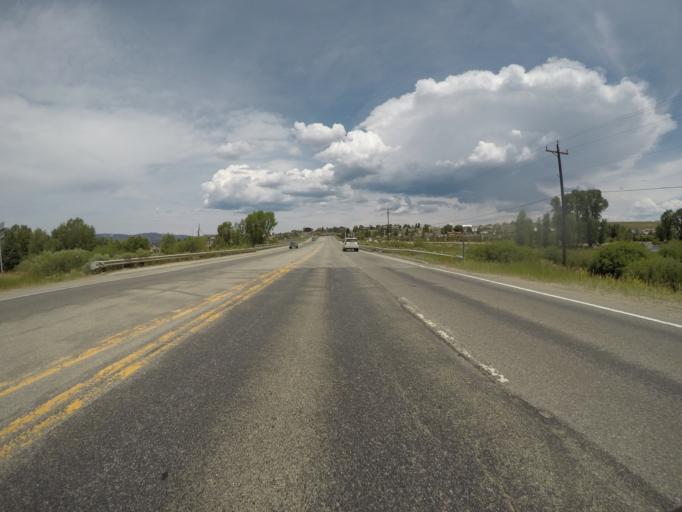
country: US
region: Colorado
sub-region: Grand County
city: Granby
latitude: 40.0809
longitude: -105.9292
